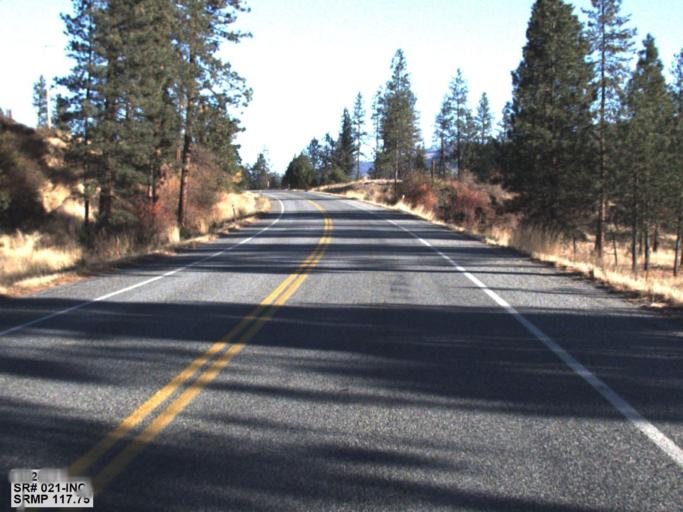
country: US
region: Washington
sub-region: Okanogan County
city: Coulee Dam
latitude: 48.0912
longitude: -118.6918
